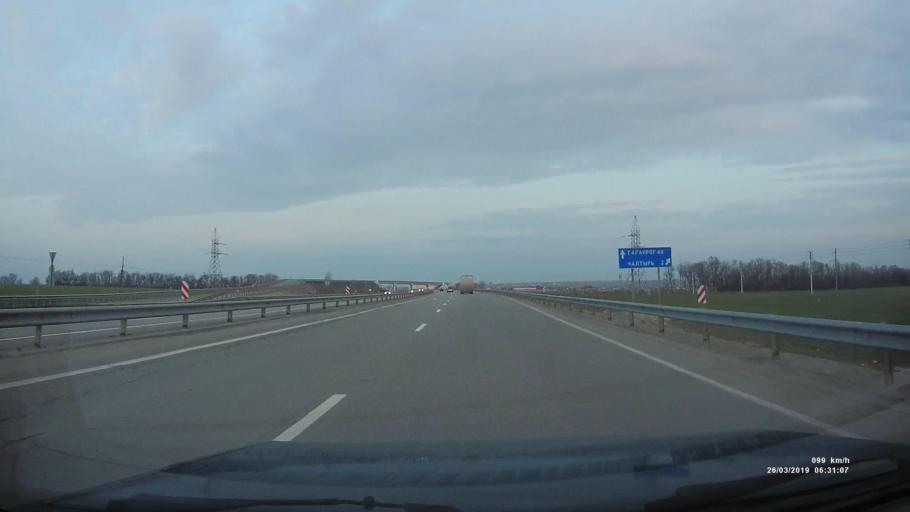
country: RU
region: Rostov
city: Krym
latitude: 47.2729
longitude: 39.5391
